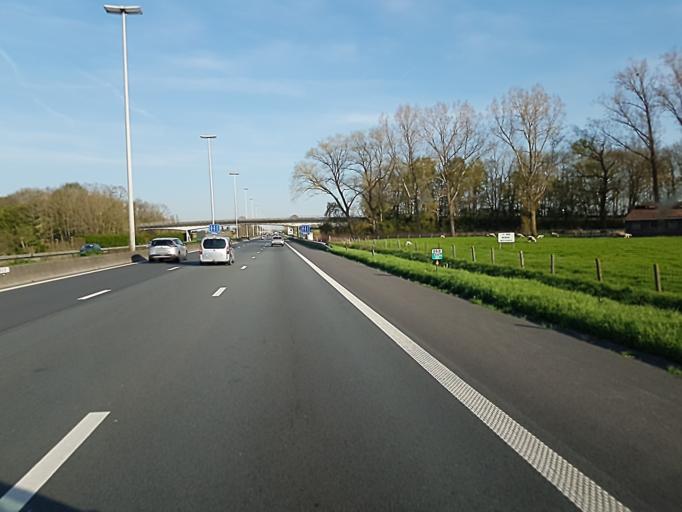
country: BE
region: Flanders
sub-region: Provincie Oost-Vlaanderen
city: Aalter
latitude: 51.0867
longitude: 3.4202
